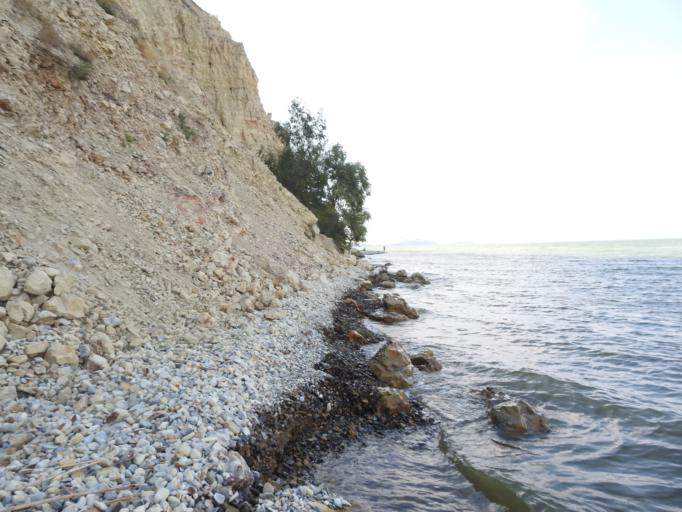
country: RU
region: Saratov
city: Rovnoye
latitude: 50.4964
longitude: 45.7968
